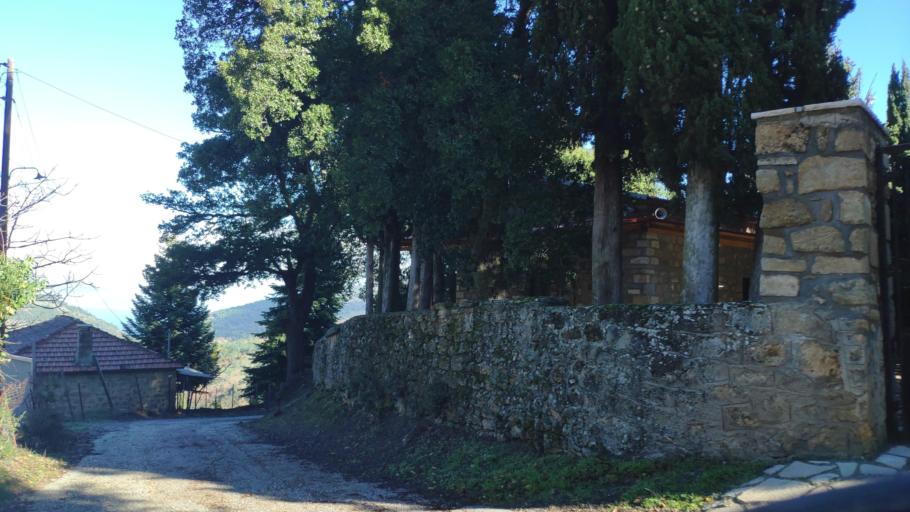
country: GR
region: West Greece
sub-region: Nomos Achaias
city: Aiyira
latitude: 38.0633
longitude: 22.4563
